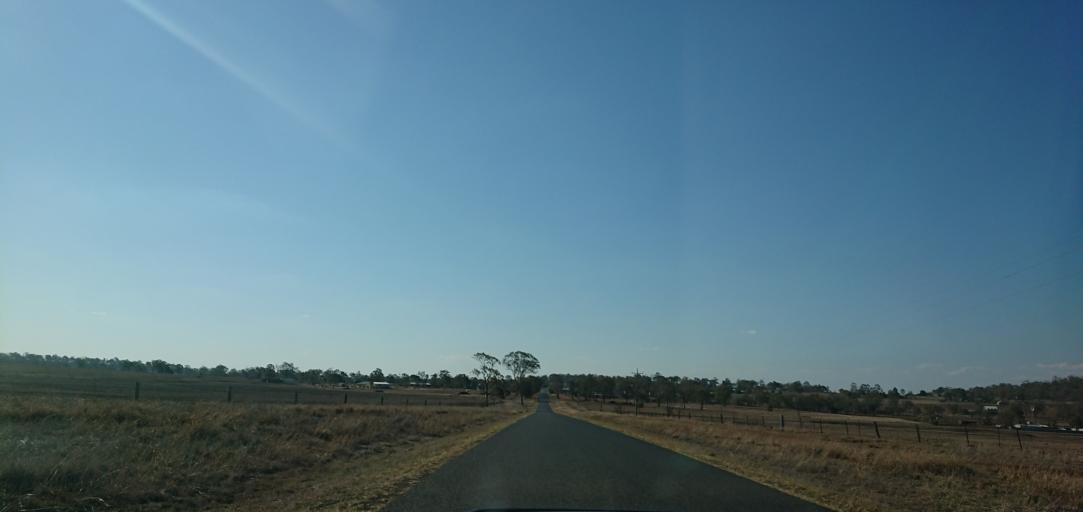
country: AU
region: Queensland
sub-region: Toowoomba
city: Westbrook
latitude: -27.6904
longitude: 151.7148
